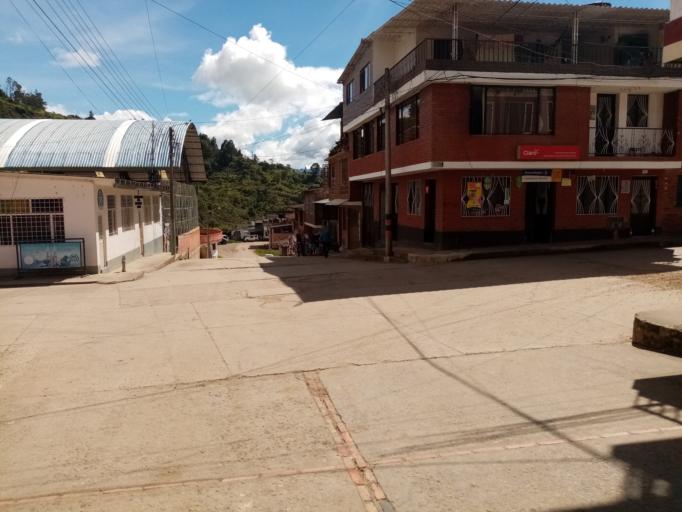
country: CO
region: Cundinamarca
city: Tenza
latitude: 5.0977
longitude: -73.4448
